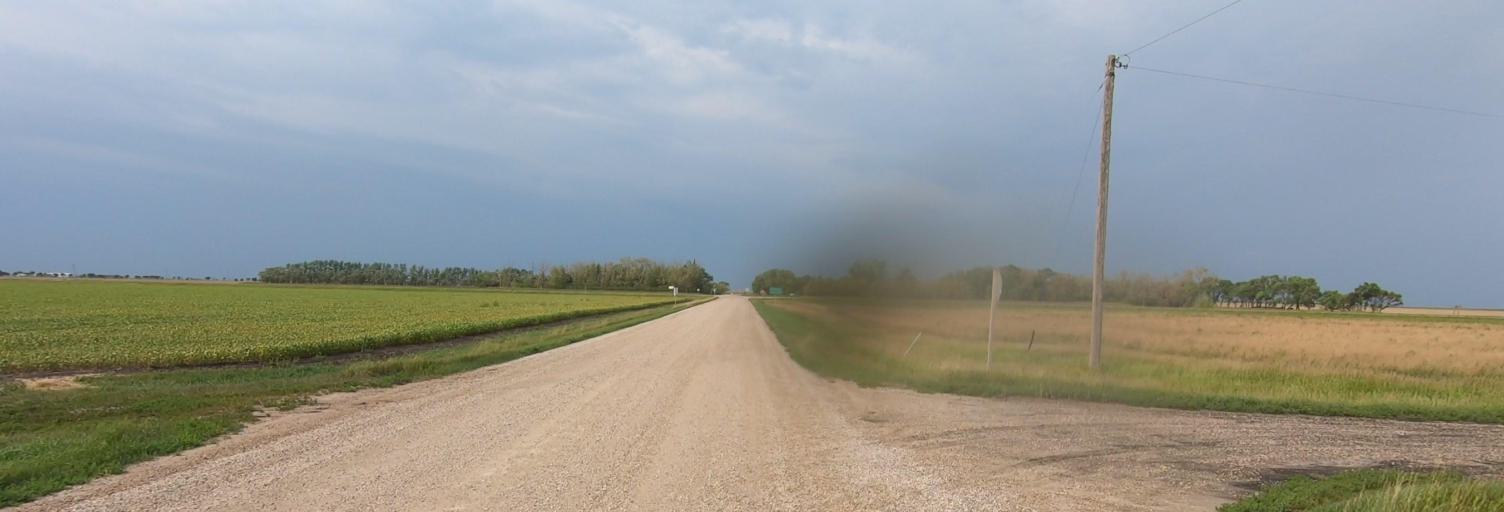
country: CA
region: Manitoba
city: Morris
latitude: 49.5765
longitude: -97.3447
